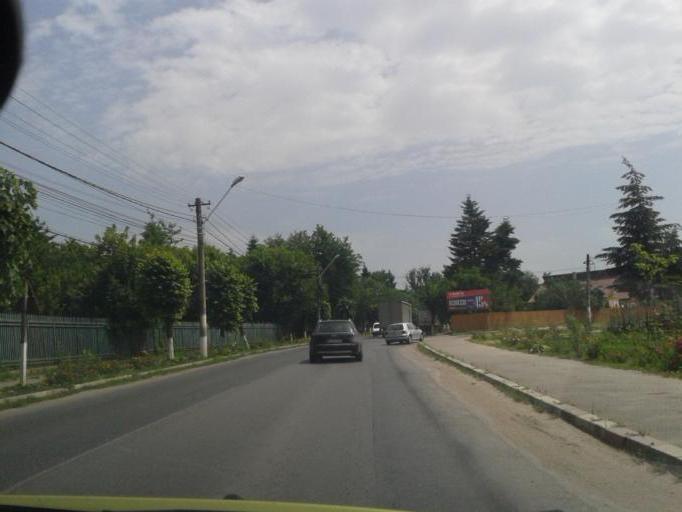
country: RO
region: Dambovita
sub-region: Oras Gaesti
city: Gaesti
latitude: 44.7157
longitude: 25.3125
